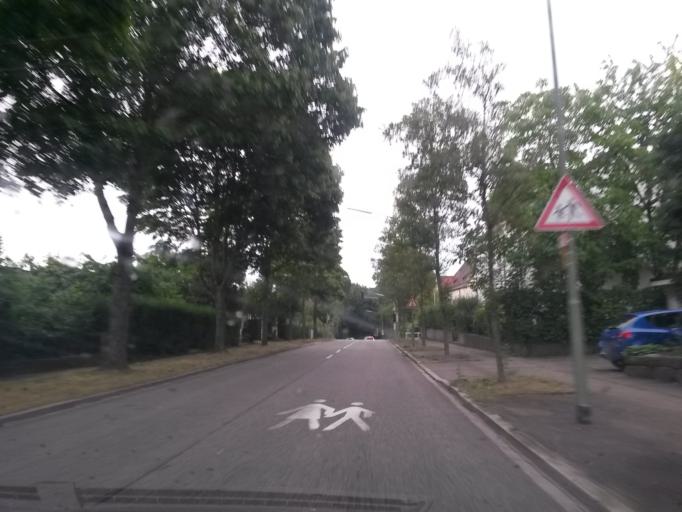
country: DE
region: Baden-Wuerttemberg
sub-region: Karlsruhe Region
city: Pforzheim
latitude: 48.8761
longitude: 8.6714
